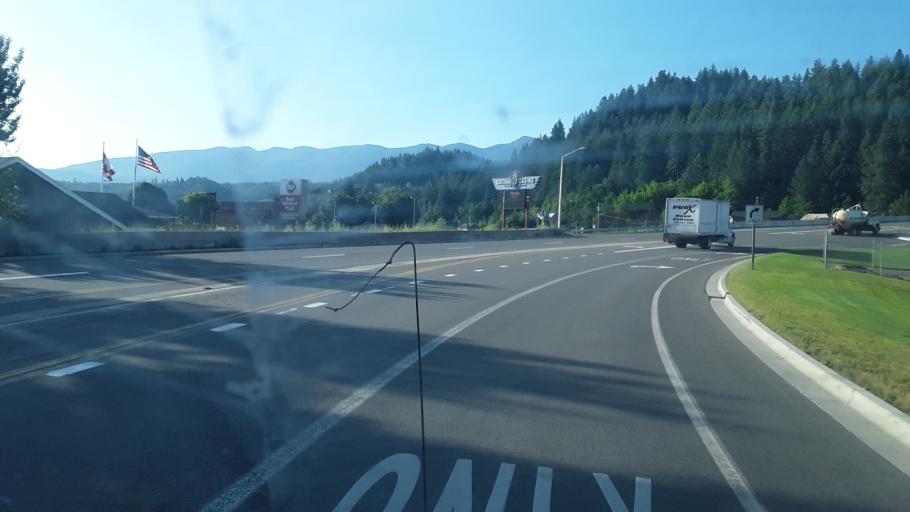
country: US
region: Idaho
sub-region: Boundary County
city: Bonners Ferry
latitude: 48.6973
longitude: -116.3099
